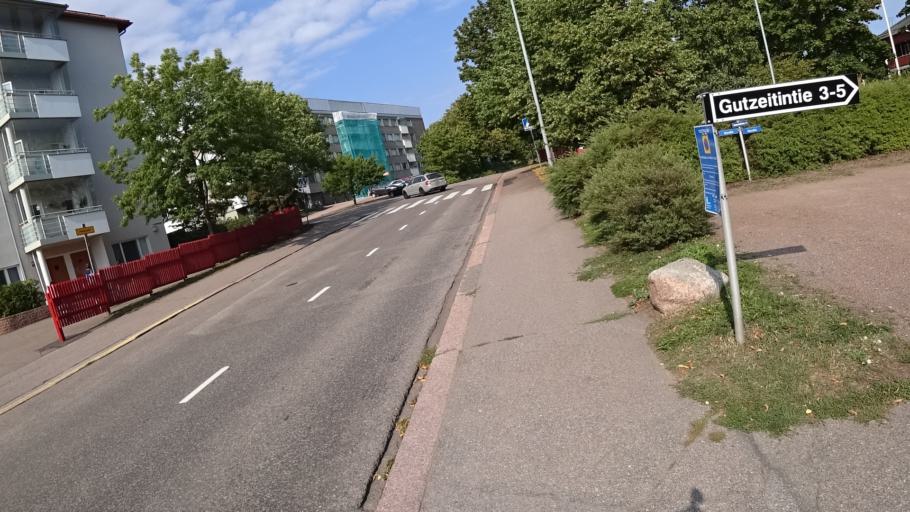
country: FI
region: Kymenlaakso
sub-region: Kotka-Hamina
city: Kotka
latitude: 60.4642
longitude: 26.9526
